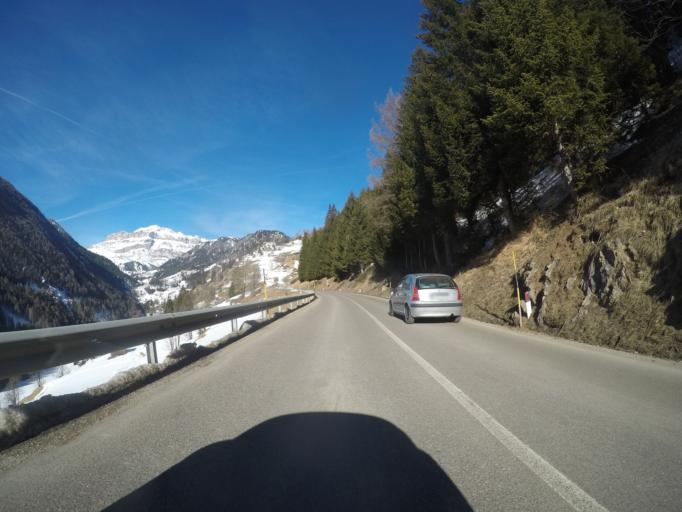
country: IT
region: Veneto
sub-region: Provincia di Belluno
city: Livinallongo del Col di Lana
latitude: 46.4929
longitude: 11.9343
